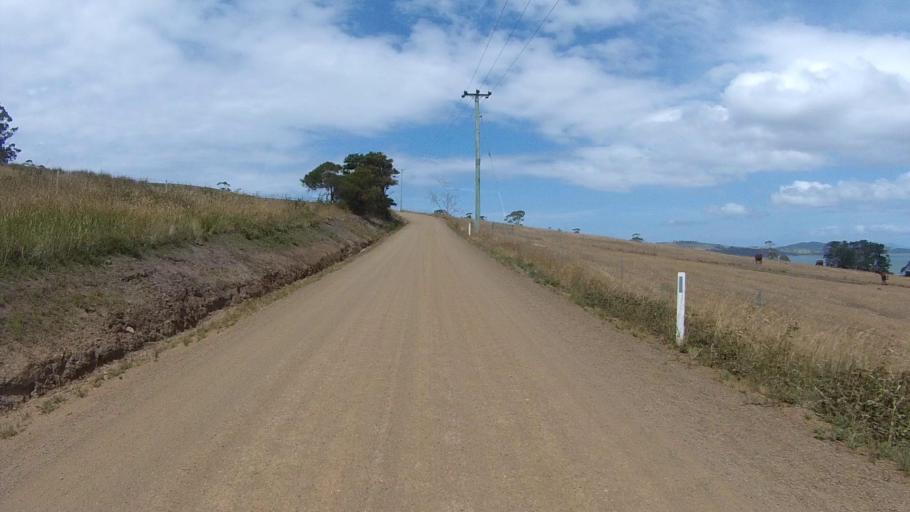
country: AU
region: Tasmania
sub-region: Kingborough
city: Blackmans Bay
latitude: -43.0541
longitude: 147.3144
